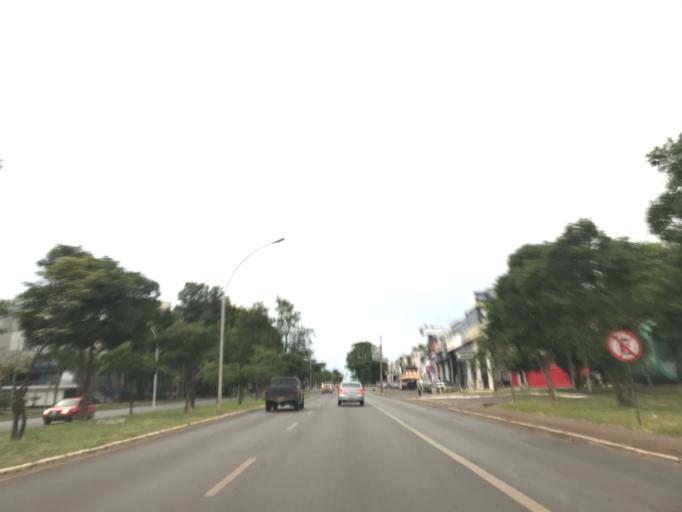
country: BR
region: Federal District
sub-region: Brasilia
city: Brasilia
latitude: -15.7418
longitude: -47.8981
